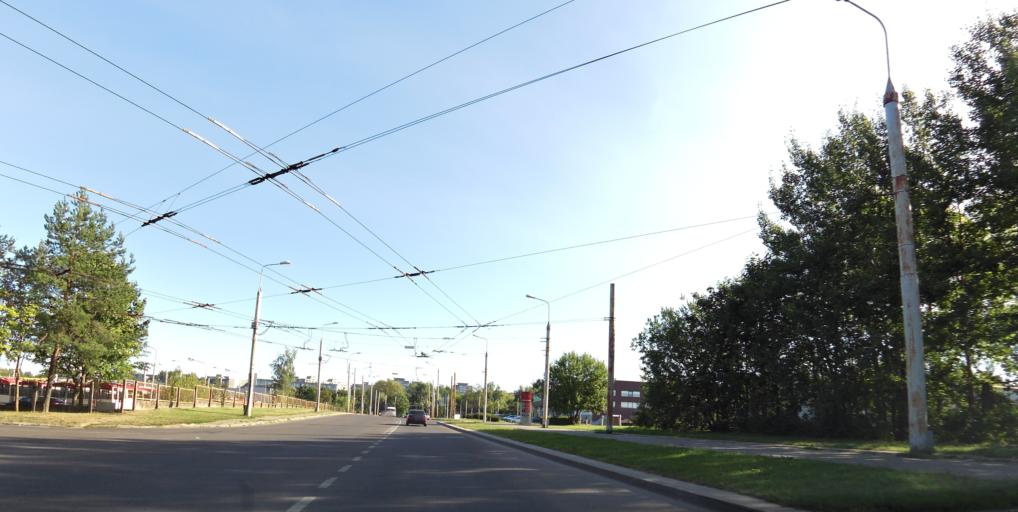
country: LT
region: Vilnius County
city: Justiniskes
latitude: 54.7021
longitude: 25.2177
